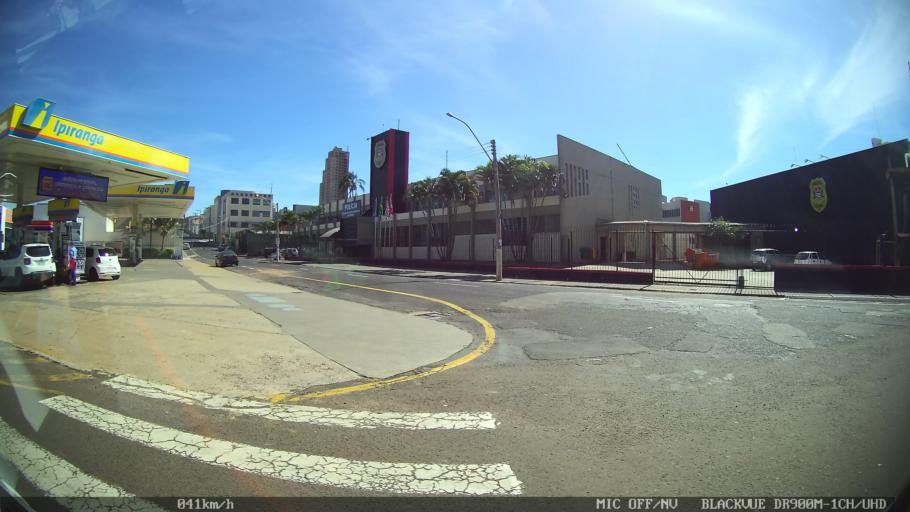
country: BR
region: Sao Paulo
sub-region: Franca
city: Franca
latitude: -20.5383
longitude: -47.3915
